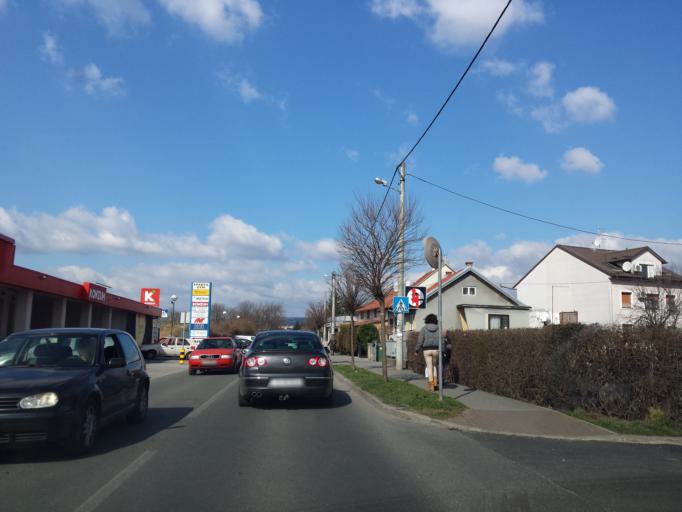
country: HR
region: Grad Zagreb
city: Jankomir
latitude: 45.8061
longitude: 15.9132
